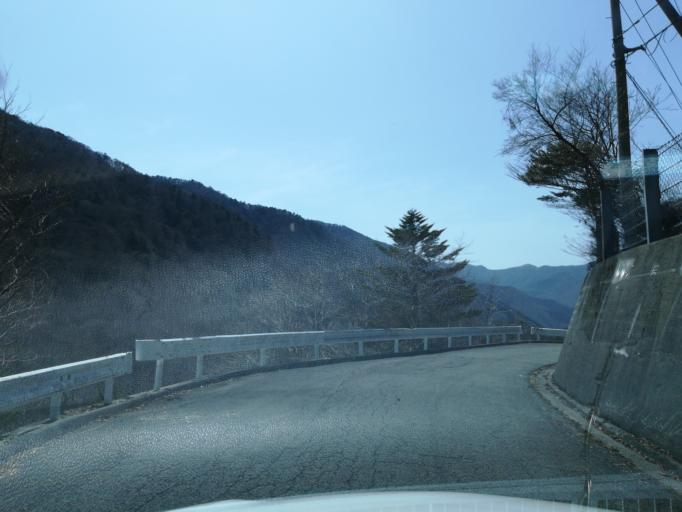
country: JP
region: Tokushima
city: Wakimachi
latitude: 33.8661
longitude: 134.0775
